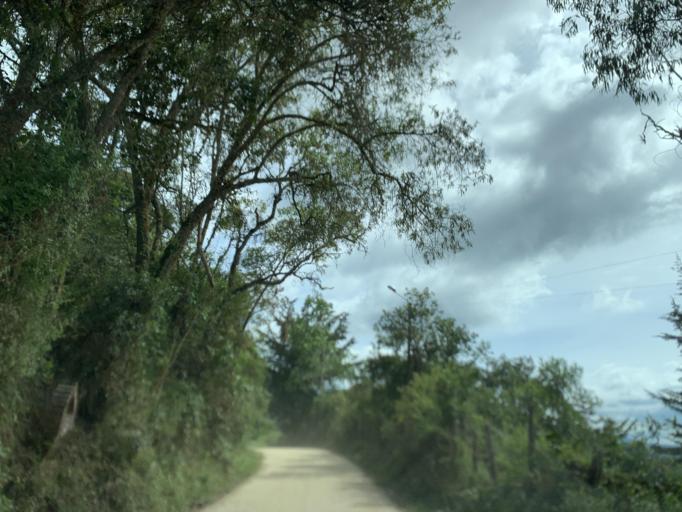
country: CO
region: Santander
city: Capitanejo
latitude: 6.5026
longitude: -72.7367
